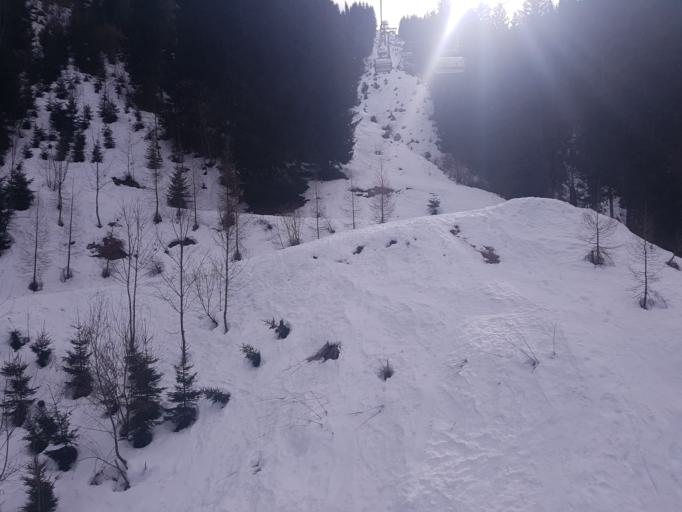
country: AT
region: Tyrol
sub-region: Politischer Bezirk Kufstein
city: Worgl
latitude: 47.4429
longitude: 12.0862
